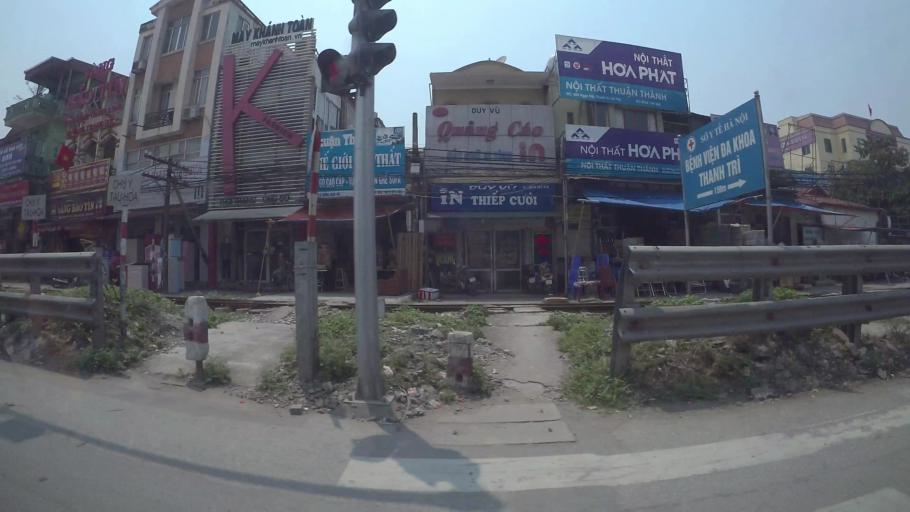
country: VN
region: Ha Noi
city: Van Dien
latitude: 20.9493
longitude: 105.8443
